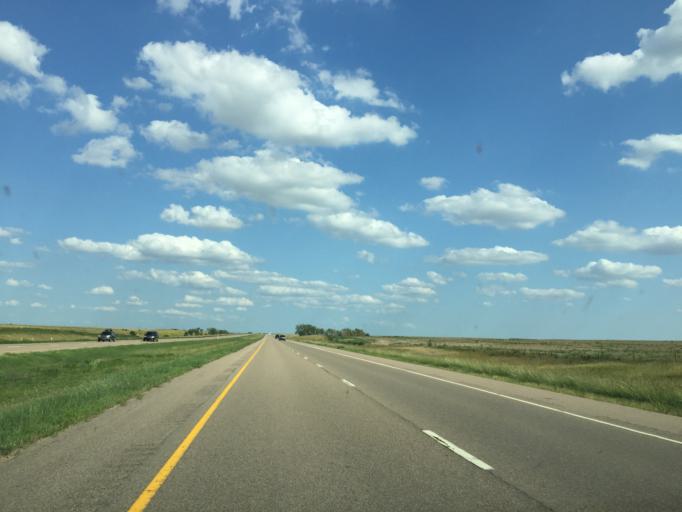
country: US
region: Kansas
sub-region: Gove County
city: Gove
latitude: 39.0946
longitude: -100.3198
